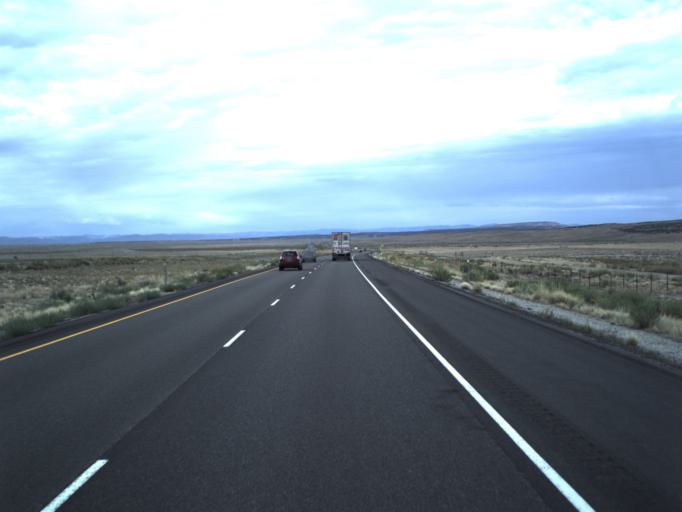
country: US
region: Colorado
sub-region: Mesa County
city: Loma
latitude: 39.0619
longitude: -109.2513
